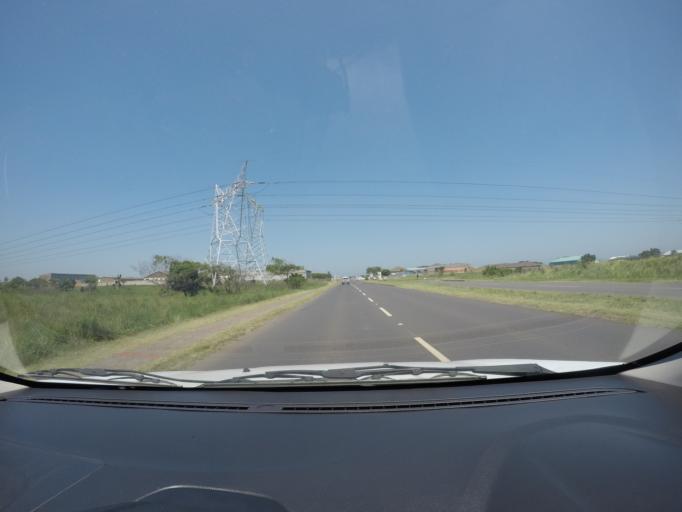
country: ZA
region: KwaZulu-Natal
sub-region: uThungulu District Municipality
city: Richards Bay
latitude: -28.7558
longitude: 32.0410
